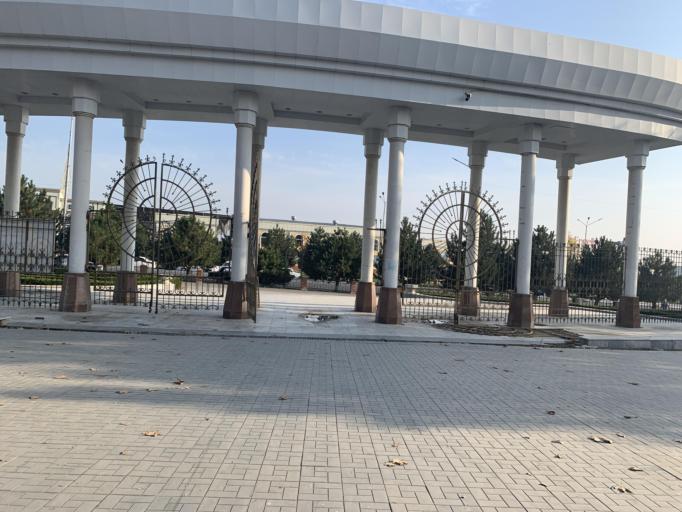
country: UZ
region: Namangan
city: Namangan Shahri
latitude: 40.9985
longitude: 71.5971
